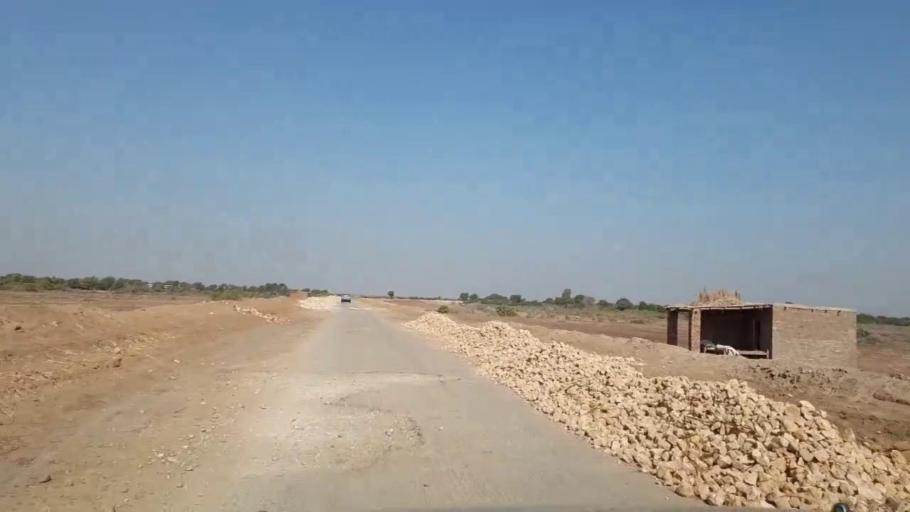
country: PK
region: Sindh
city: Digri
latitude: 24.9634
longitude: 69.1130
